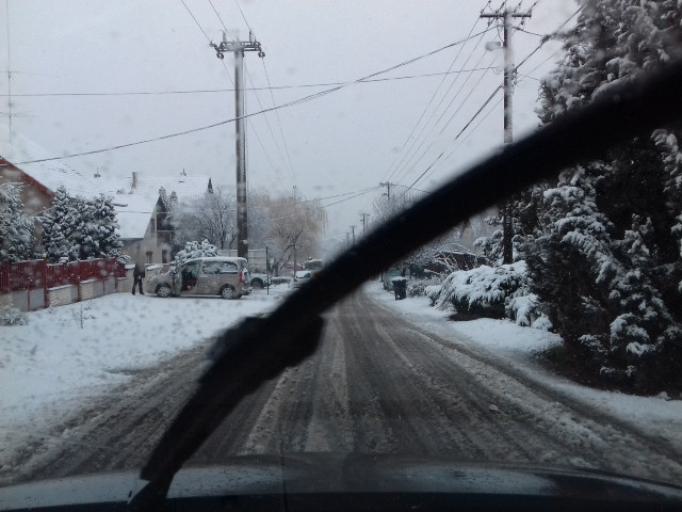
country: HU
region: Pest
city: Fot
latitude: 47.6273
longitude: 19.1902
